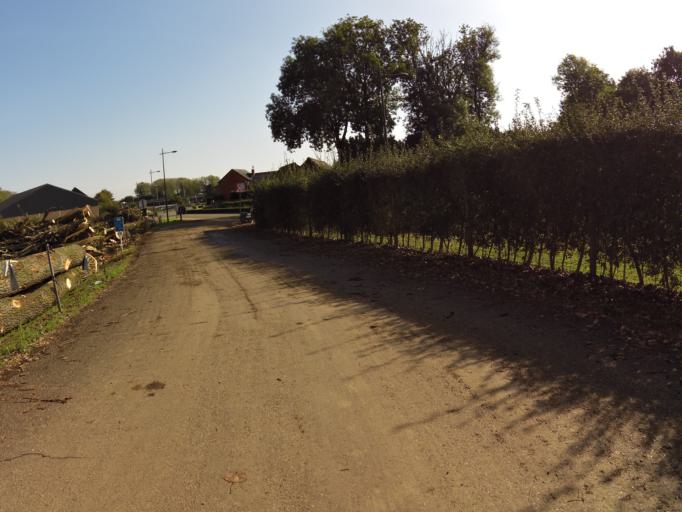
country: NL
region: Limburg
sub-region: Gemeente Stein
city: Stein
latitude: 50.9550
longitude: 5.7354
